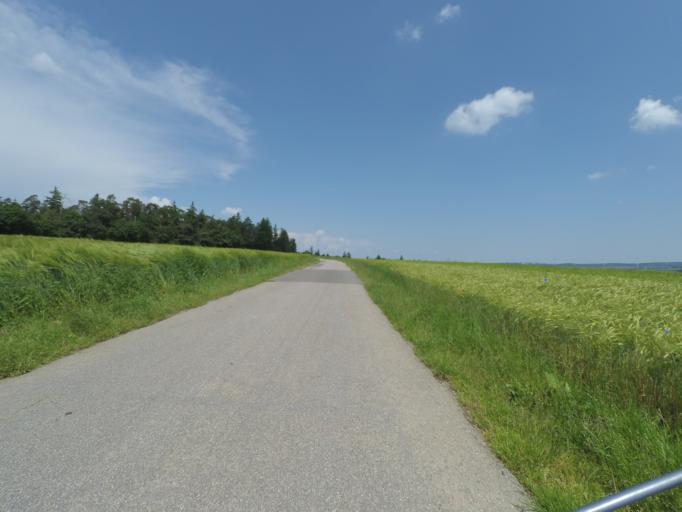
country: DE
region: Rheinland-Pfalz
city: Mermuth
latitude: 50.1658
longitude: 7.4951
